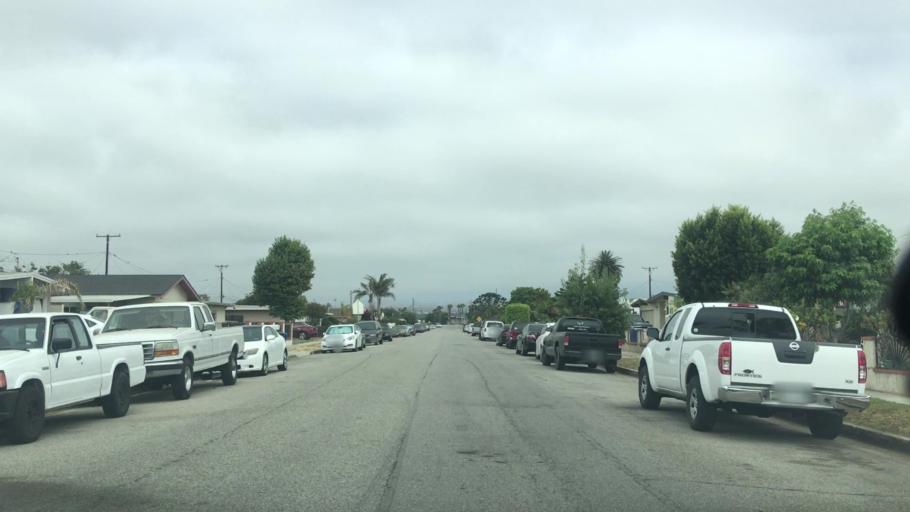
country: US
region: California
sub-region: Ventura County
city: El Rio
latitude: 34.2414
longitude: -119.1600
